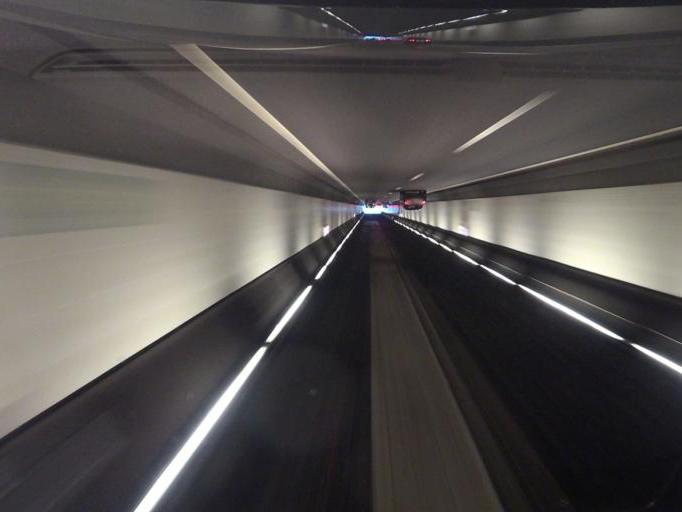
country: NL
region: North Holland
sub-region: Gemeente Velsen
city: Velsen-Zuid
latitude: 52.4634
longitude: 4.6532
